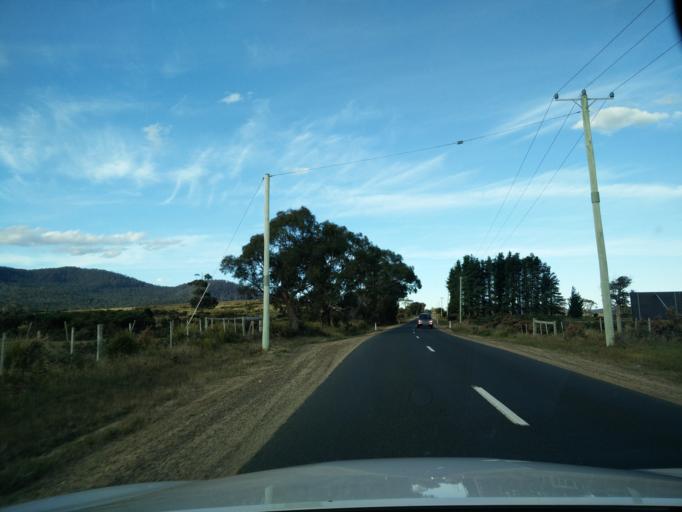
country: AU
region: Tasmania
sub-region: Break O'Day
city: St Helens
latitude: -41.9371
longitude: 148.2222
